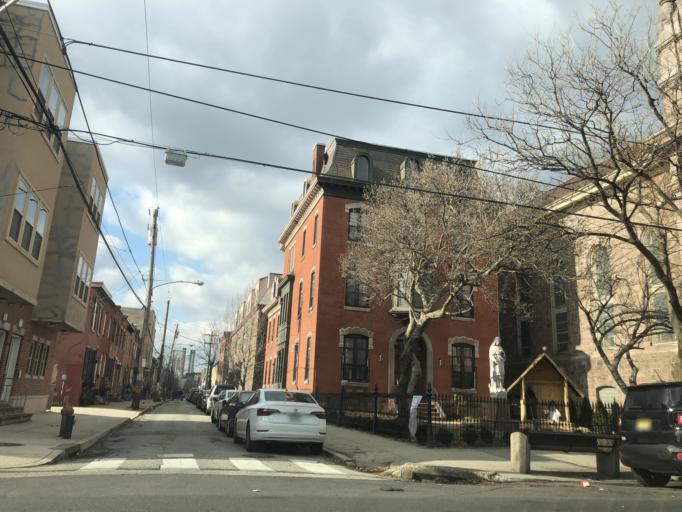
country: US
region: Pennsylvania
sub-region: Philadelphia County
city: Philadelphia
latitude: 39.9408
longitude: -75.1758
